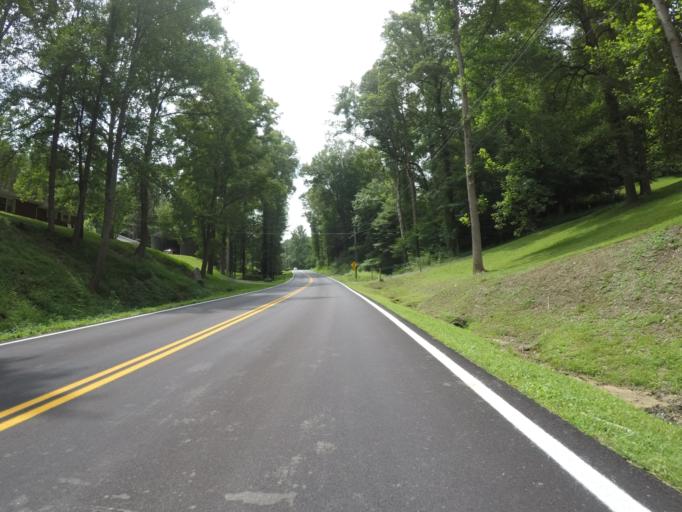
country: US
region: Kentucky
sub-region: Boyd County
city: Catlettsburg
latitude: 38.4319
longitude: -82.6291
